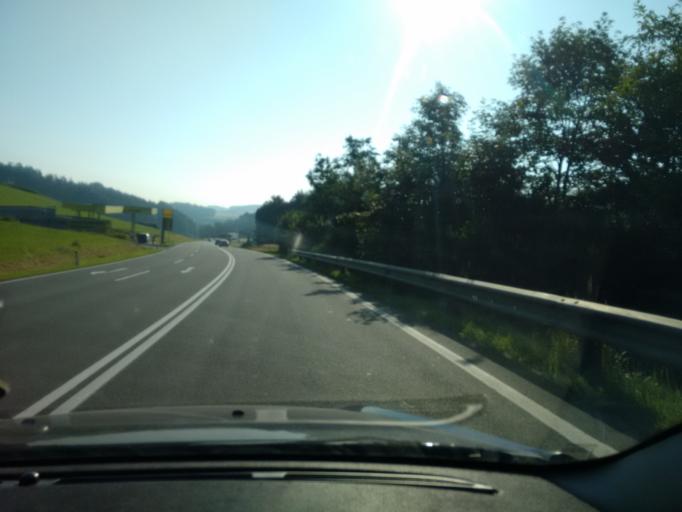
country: AT
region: Upper Austria
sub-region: Politischer Bezirk Vocklabruck
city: Attnang-Puchheim
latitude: 47.9546
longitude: 13.7355
